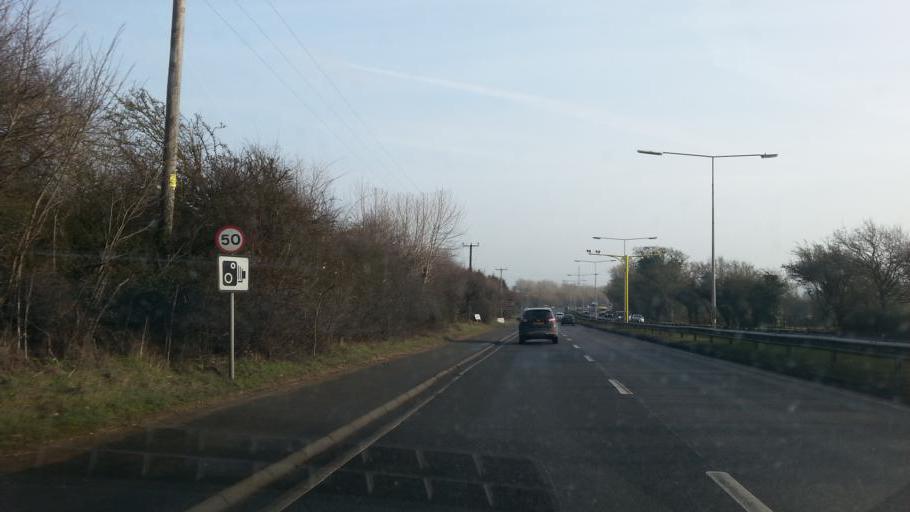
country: GB
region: England
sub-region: Essex
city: Wickford
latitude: 51.5893
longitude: 0.5468
